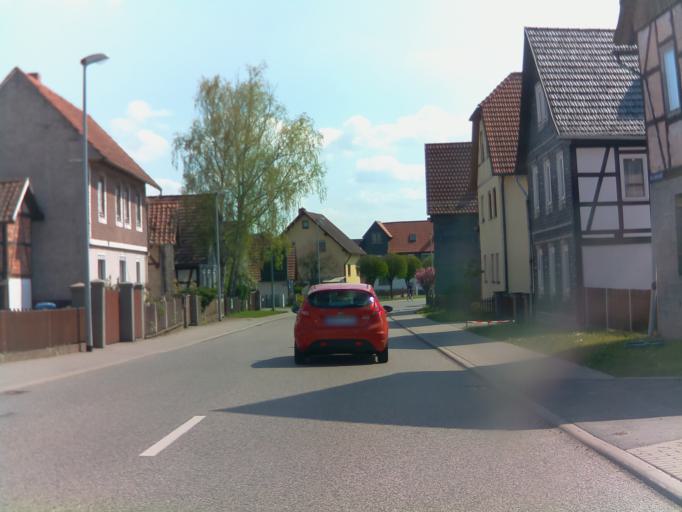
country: DE
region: Thuringia
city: Westhausen
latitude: 50.3569
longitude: 10.6858
